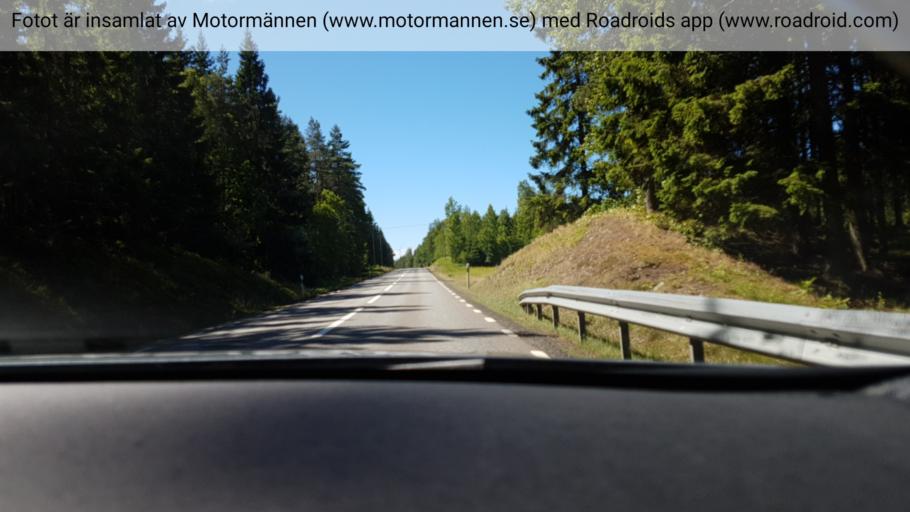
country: SE
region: Joenkoeping
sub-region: Mullsjo Kommun
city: Mullsjoe
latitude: 57.7950
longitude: 13.8418
